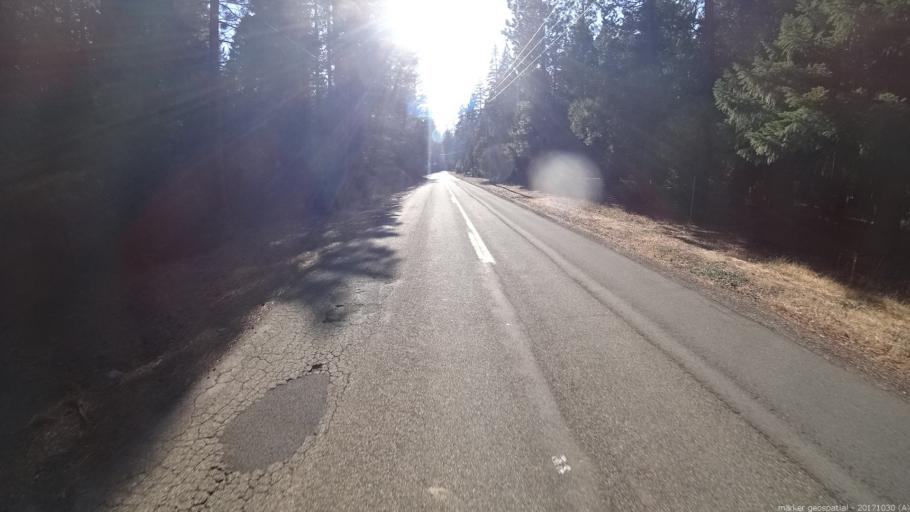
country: US
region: California
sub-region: Shasta County
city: Shingletown
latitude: 40.5192
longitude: -121.7530
